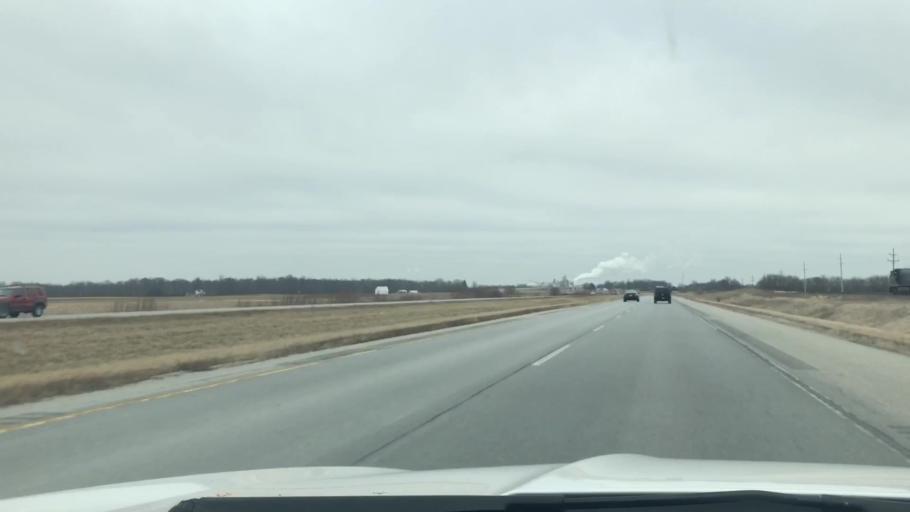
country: US
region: Indiana
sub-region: Cass County
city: Georgetown
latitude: 40.6970
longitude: -86.4691
